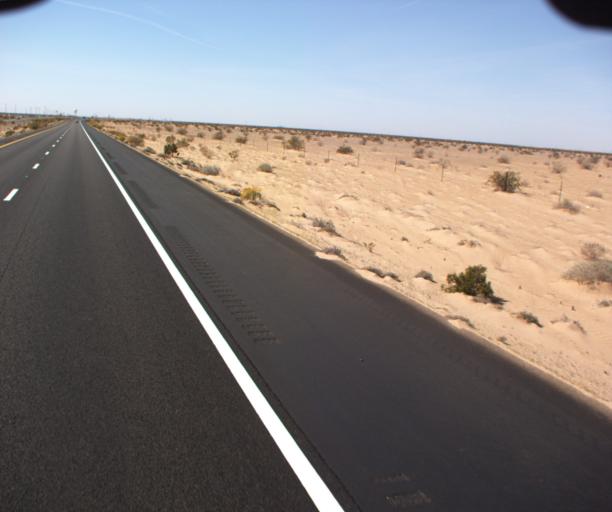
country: US
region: Arizona
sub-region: Yuma County
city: Somerton
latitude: 32.4954
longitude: -114.6336
